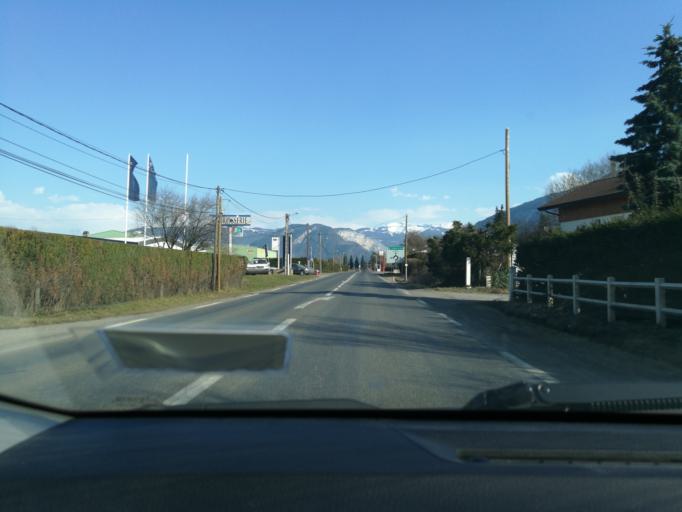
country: FR
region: Rhone-Alpes
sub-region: Departement de la Haute-Savoie
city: Vougy
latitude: 46.0667
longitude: 6.5095
